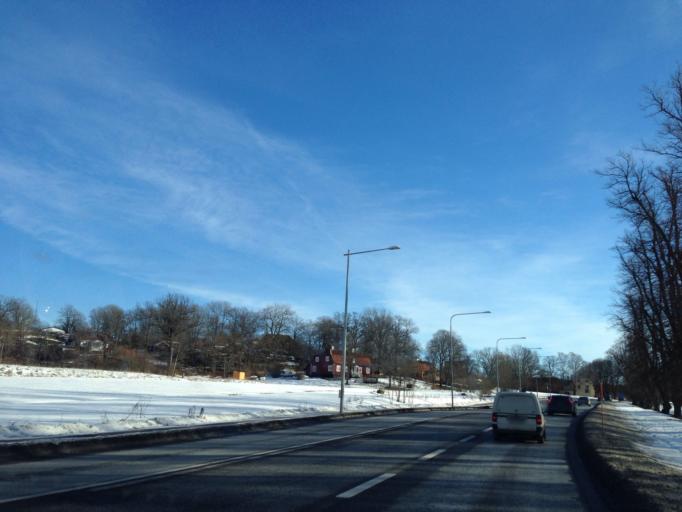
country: SE
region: Stockholm
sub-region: Stockholms Kommun
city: Bromma
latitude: 59.3263
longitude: 17.8810
